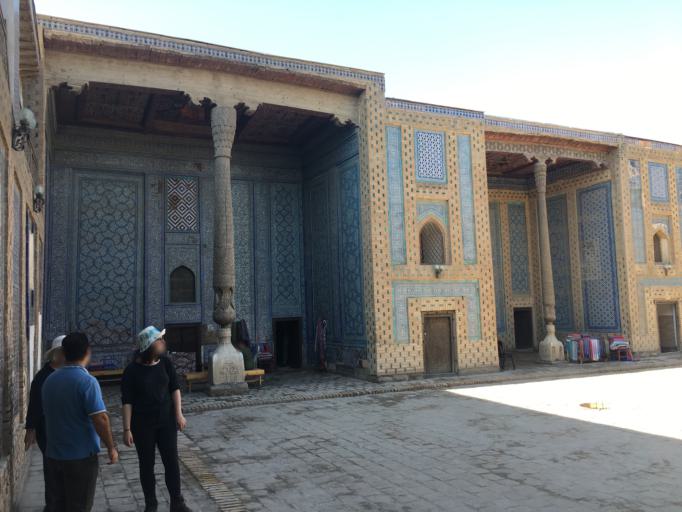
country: UZ
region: Xorazm
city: Khiwa
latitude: 41.3784
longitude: 60.3619
